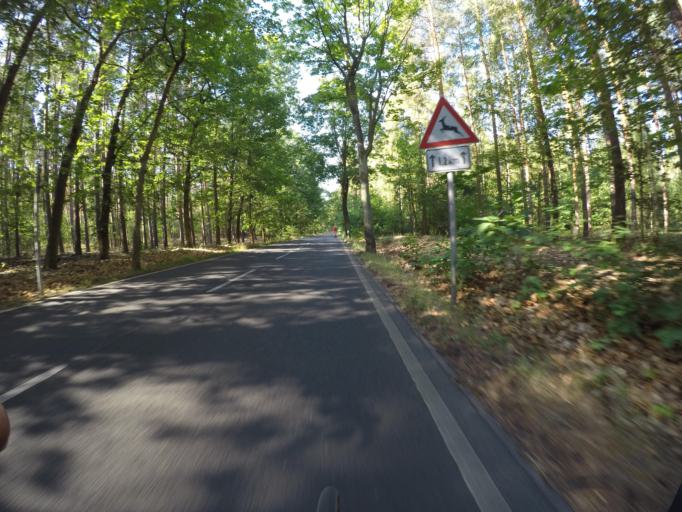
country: DE
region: Berlin
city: Schmockwitz
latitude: 52.3620
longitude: 13.6529
